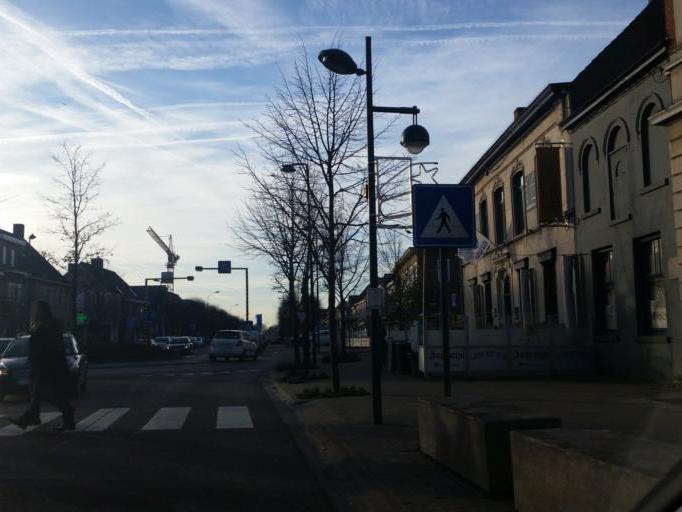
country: BE
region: Flanders
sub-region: Provincie Oost-Vlaanderen
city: Assenede
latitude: 51.1791
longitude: 3.7468
